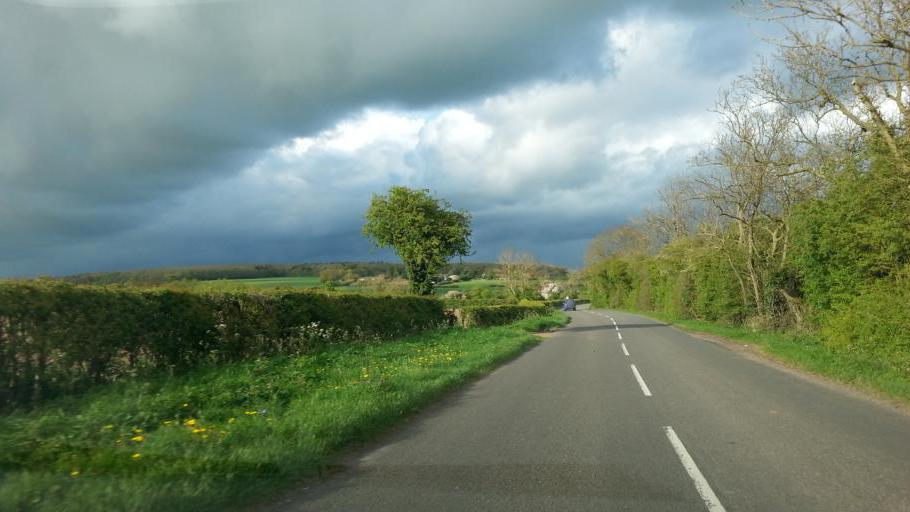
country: GB
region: England
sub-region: Nottinghamshire
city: Southwell
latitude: 53.1051
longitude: -0.9284
